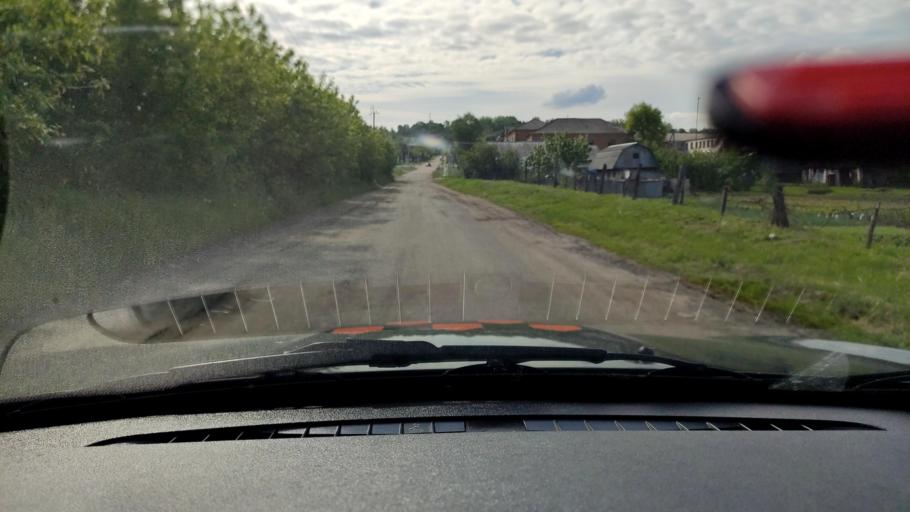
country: RU
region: Voronezj
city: Uryv-Pokrovka
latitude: 51.1109
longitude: 39.1612
